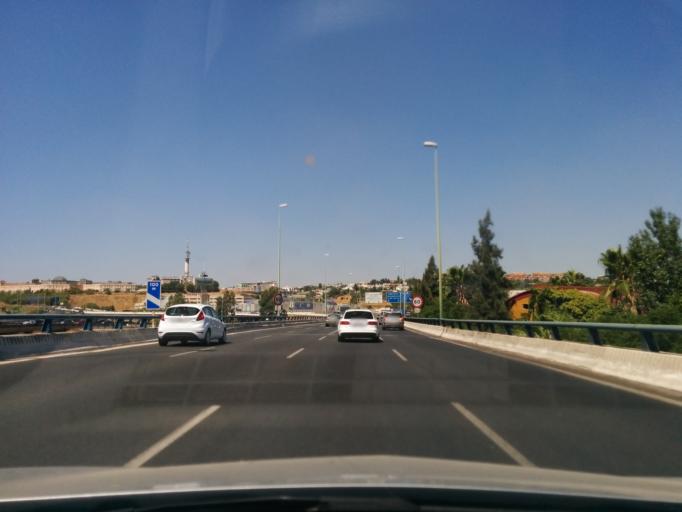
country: ES
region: Andalusia
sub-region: Provincia de Sevilla
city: San Juan de Aznalfarache
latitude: 37.3724
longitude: -6.0241
